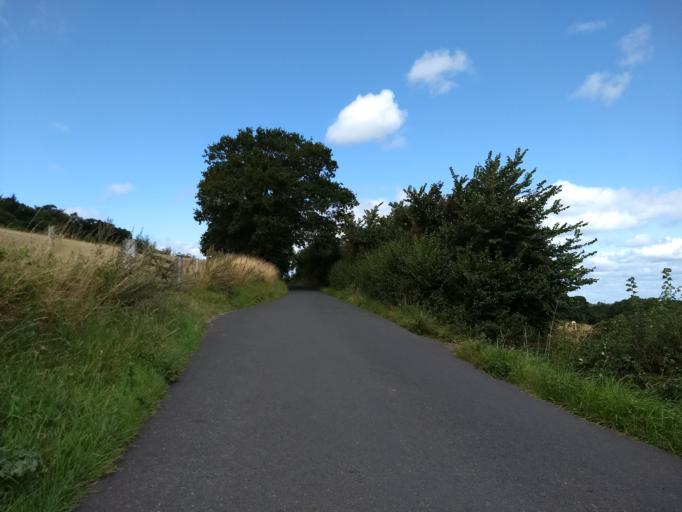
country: GB
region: England
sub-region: Isle of Wight
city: Newport
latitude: 50.6775
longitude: -1.2911
